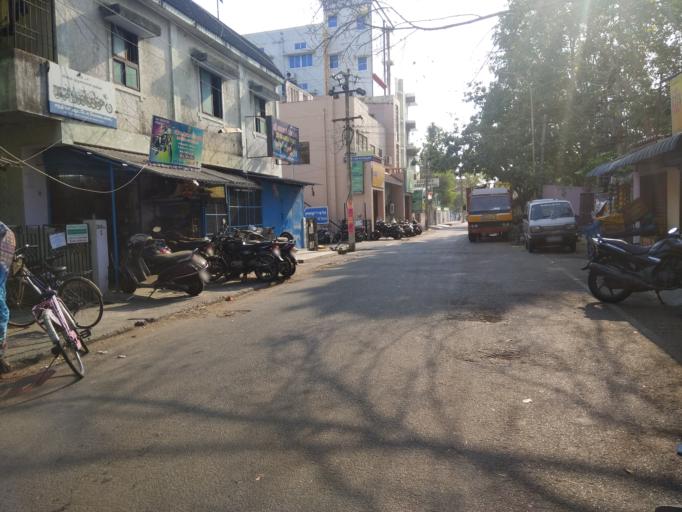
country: IN
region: Tamil Nadu
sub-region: Kancheepuram
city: Saint Thomas Mount
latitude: 12.9839
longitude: 80.1881
